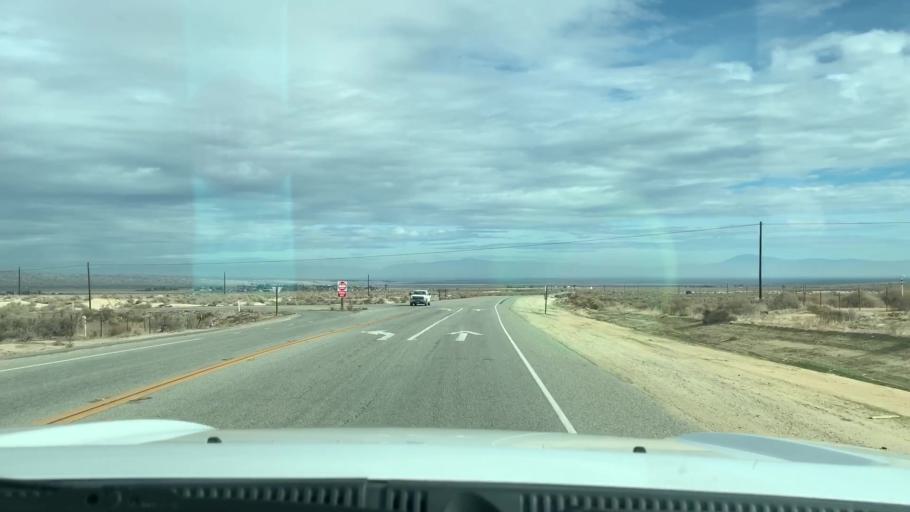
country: US
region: California
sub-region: Kern County
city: Ford City
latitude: 35.1864
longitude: -119.4464
